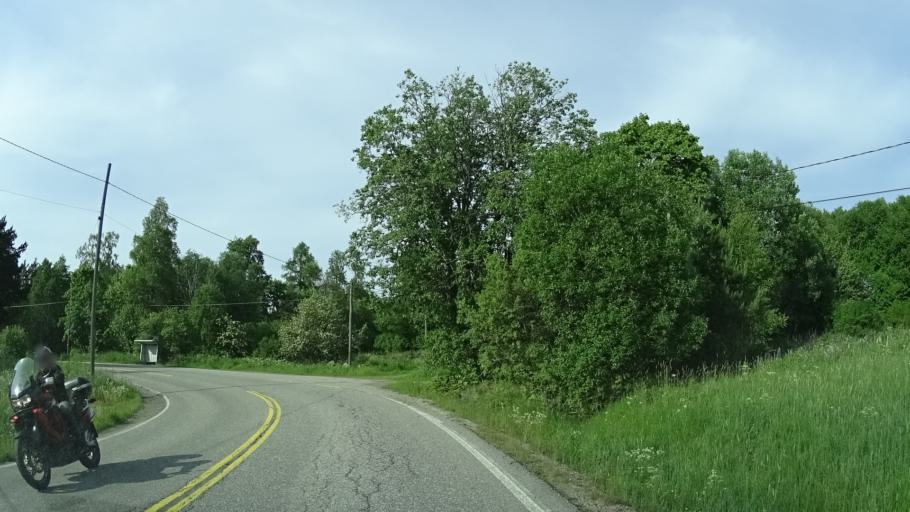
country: FI
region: Uusimaa
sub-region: Helsinki
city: Kirkkonummi
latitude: 60.0975
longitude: 24.4990
